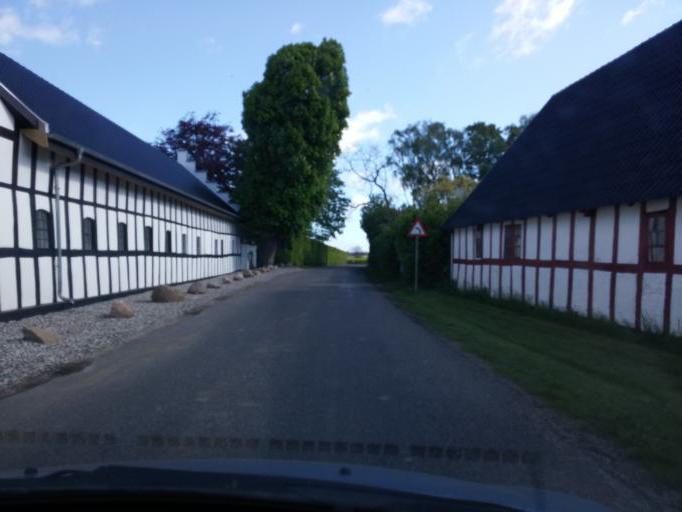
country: DK
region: South Denmark
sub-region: Kerteminde Kommune
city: Munkebo
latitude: 55.4099
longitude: 10.5436
